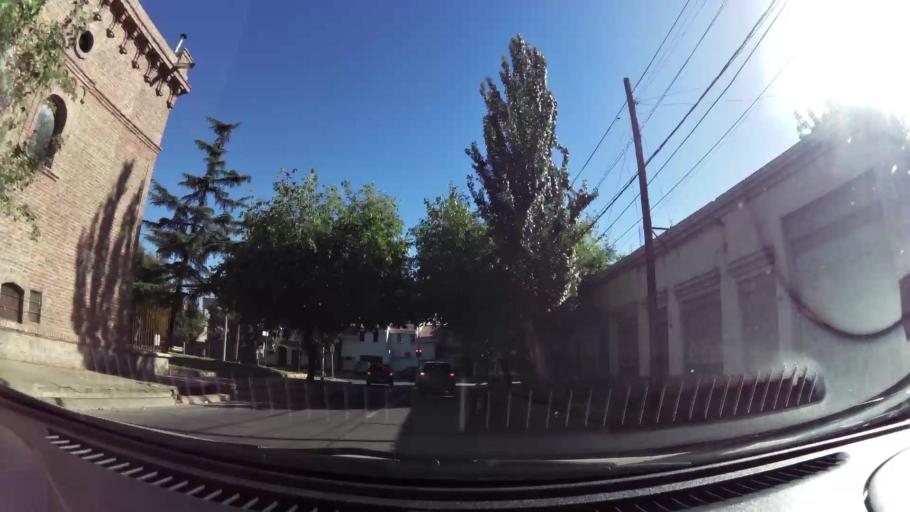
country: AR
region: Mendoza
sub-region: Departamento de Godoy Cruz
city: Godoy Cruz
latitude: -32.9126
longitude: -68.8423
